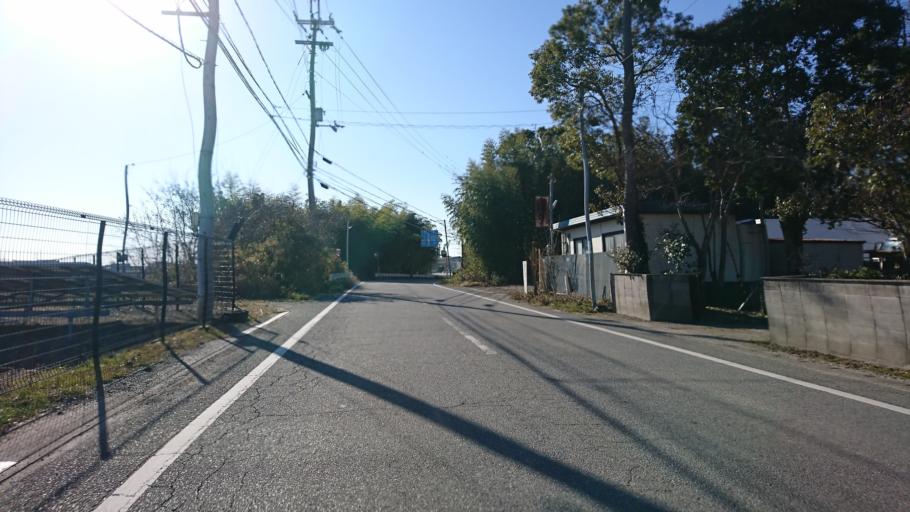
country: JP
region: Hyogo
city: Miki
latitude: 34.7543
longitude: 134.9259
